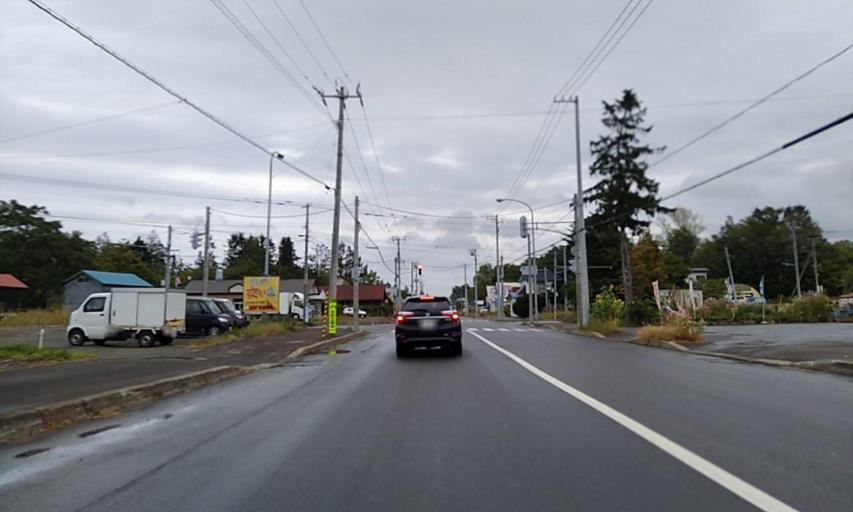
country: JP
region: Hokkaido
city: Kitami
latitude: 44.0811
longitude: 143.9443
